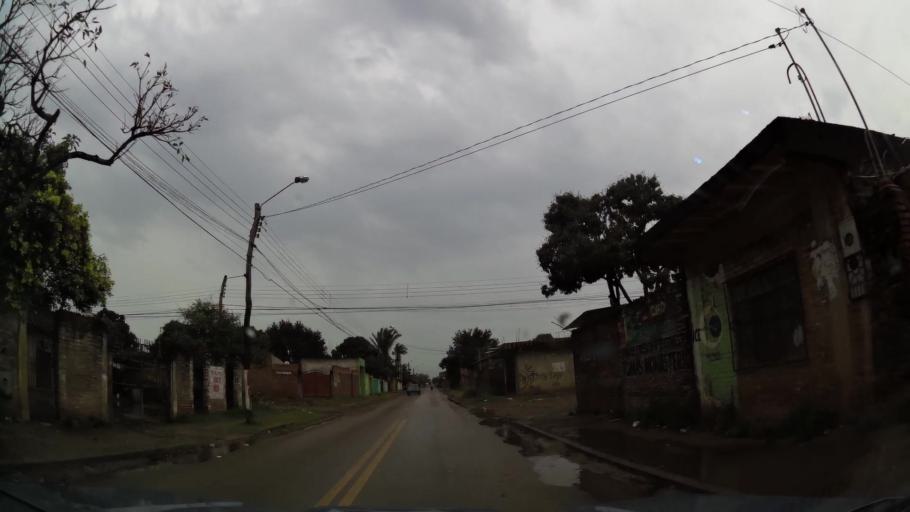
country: BO
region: Santa Cruz
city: Santa Cruz de la Sierra
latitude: -17.7575
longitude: -63.1175
